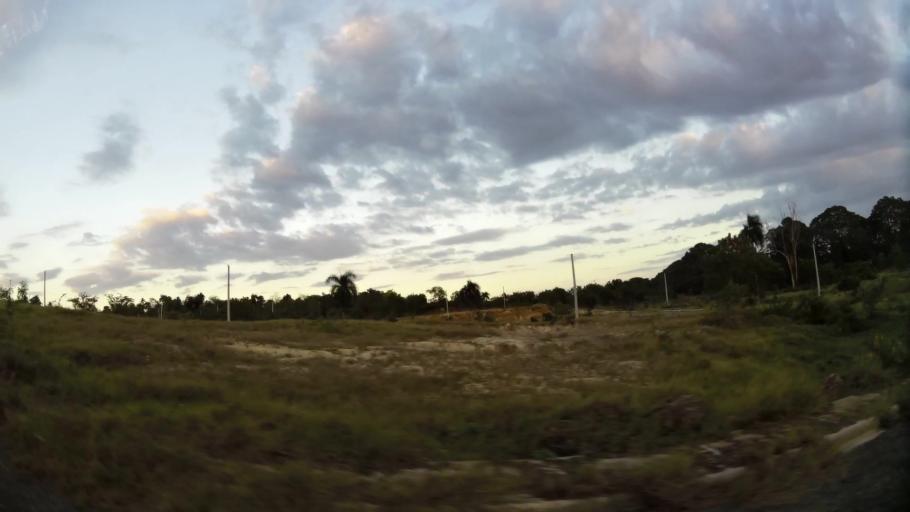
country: DO
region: Nacional
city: La Agustina
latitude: 18.5653
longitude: -69.9360
